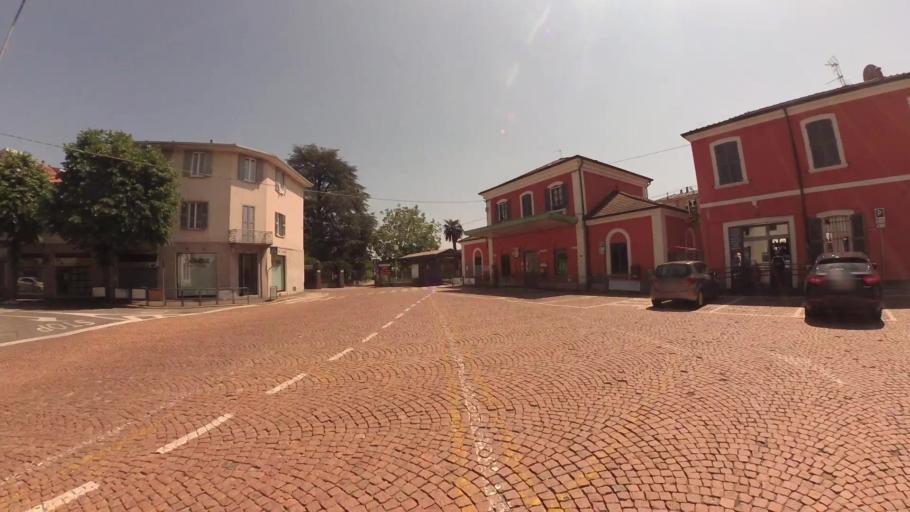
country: IT
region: Lombardy
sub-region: Provincia di Varese
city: Tradate
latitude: 45.7107
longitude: 8.9069
